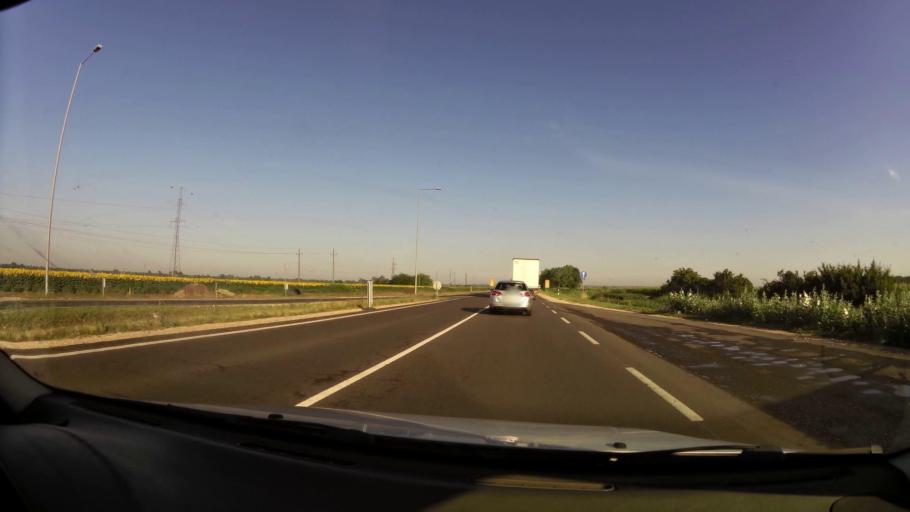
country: HU
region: Pest
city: Cegled
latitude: 47.2047
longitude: 19.7729
